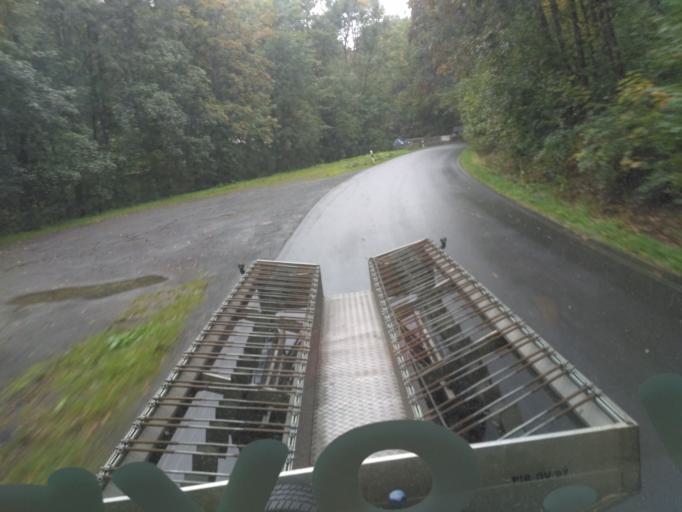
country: DE
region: Saxony
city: Konigstein
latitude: 50.8634
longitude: 14.0419
